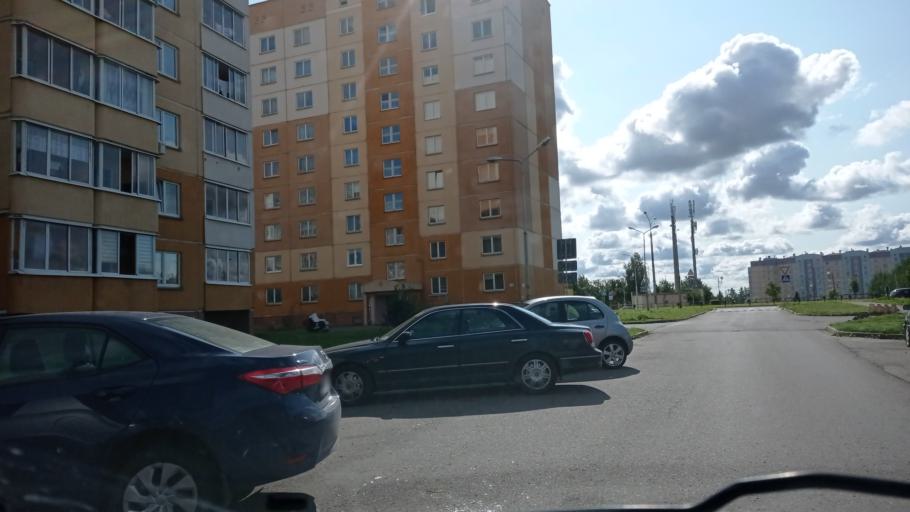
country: BY
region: Vitebsk
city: Vitebsk
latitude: 55.1699
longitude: 30.2641
